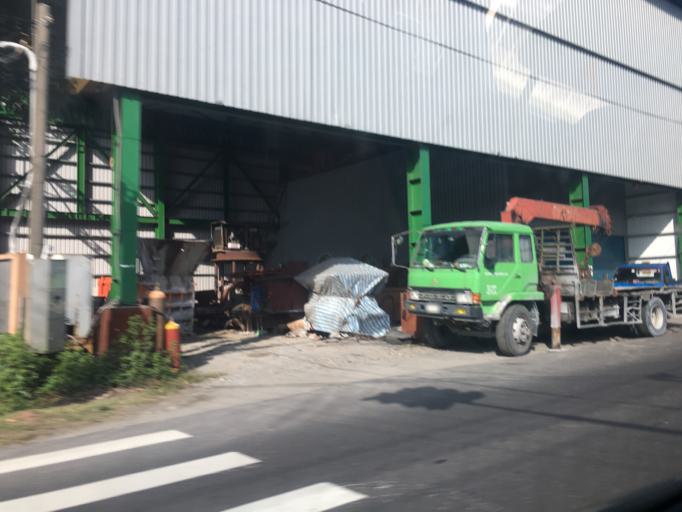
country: TW
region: Taiwan
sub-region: Yilan
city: Yilan
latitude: 24.7016
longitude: 121.7451
